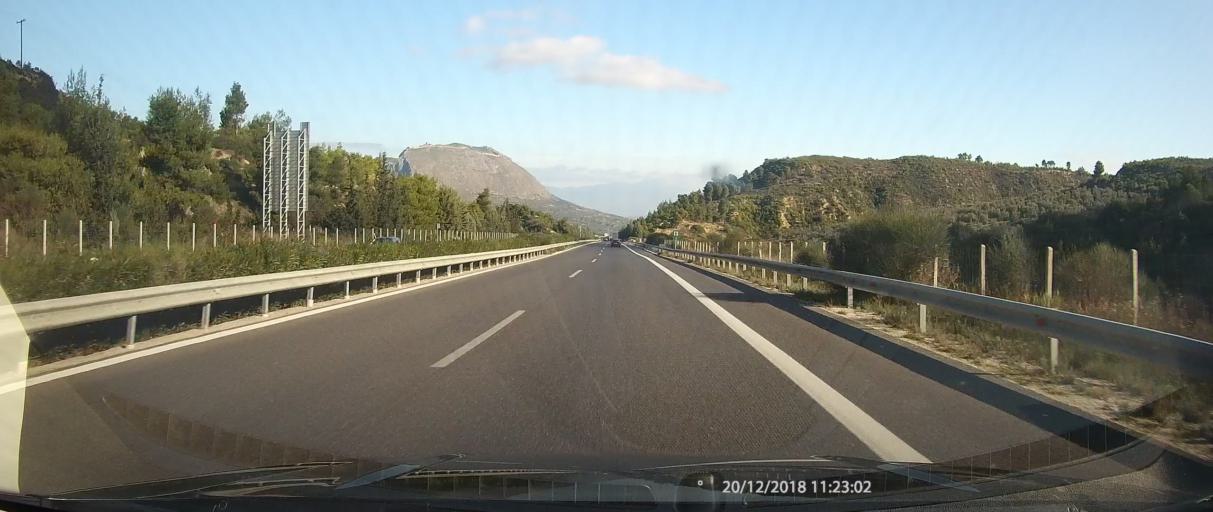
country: GR
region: Peloponnese
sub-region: Nomos Korinthias
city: Arkhaia Korinthos
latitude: 37.8658
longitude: 22.8486
